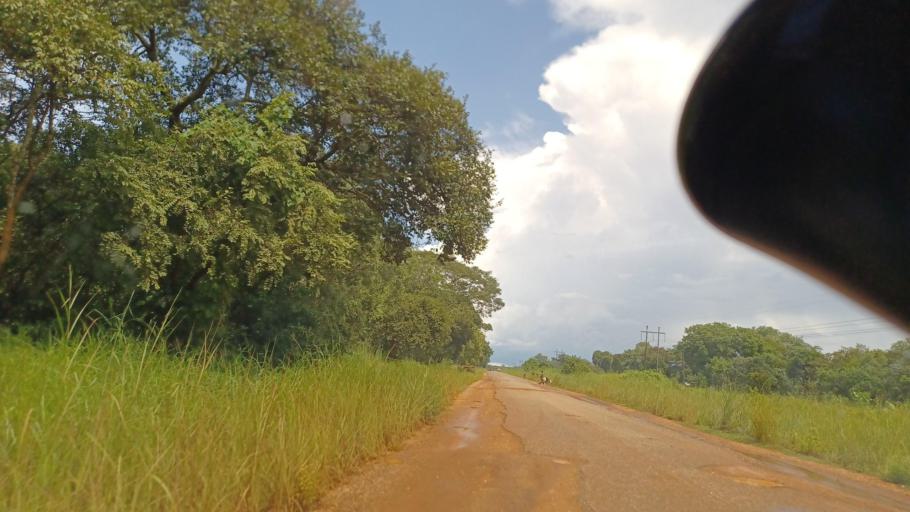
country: ZM
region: North-Western
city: Kasempa
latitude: -12.8967
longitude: 26.0535
